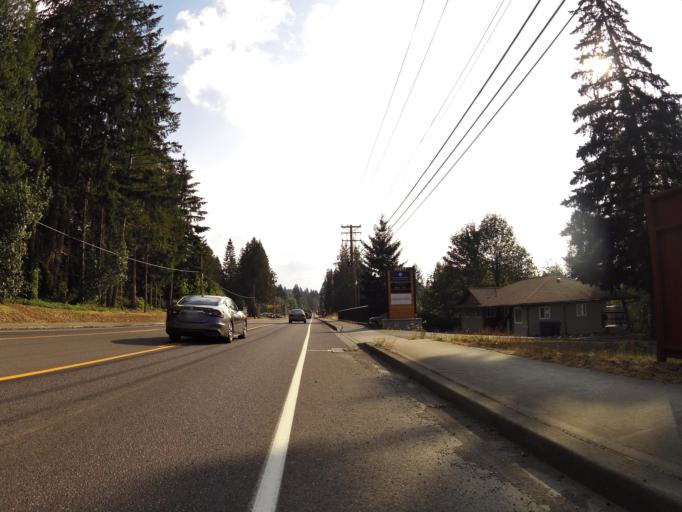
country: US
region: Washington
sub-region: Mason County
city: Belfair
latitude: 47.4435
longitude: -122.8323
